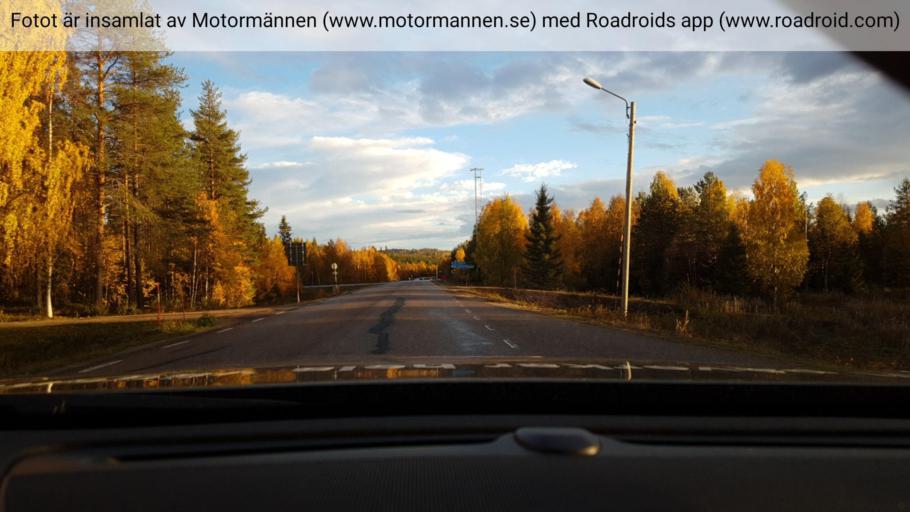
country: SE
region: Norrbotten
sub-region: Overkalix Kommun
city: OEverkalix
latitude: 66.6119
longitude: 22.7562
